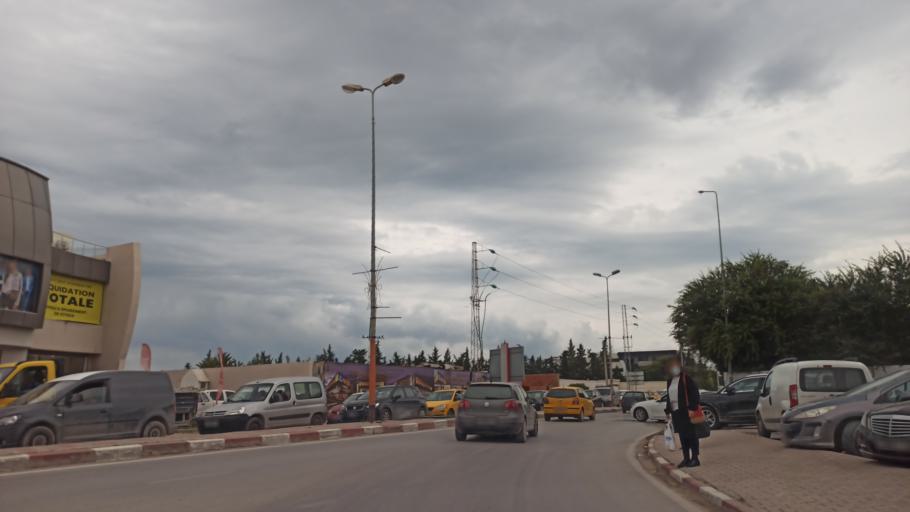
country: TN
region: Ariana
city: Ariana
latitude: 36.8748
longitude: 10.2457
